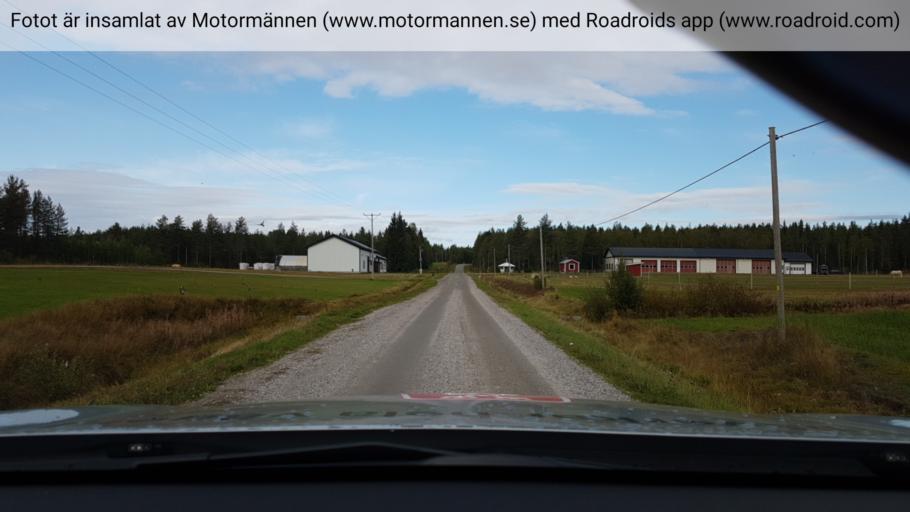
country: SE
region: Vaesterbotten
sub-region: Skelleftea Kommun
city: Backa
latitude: 65.1494
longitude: 21.1657
